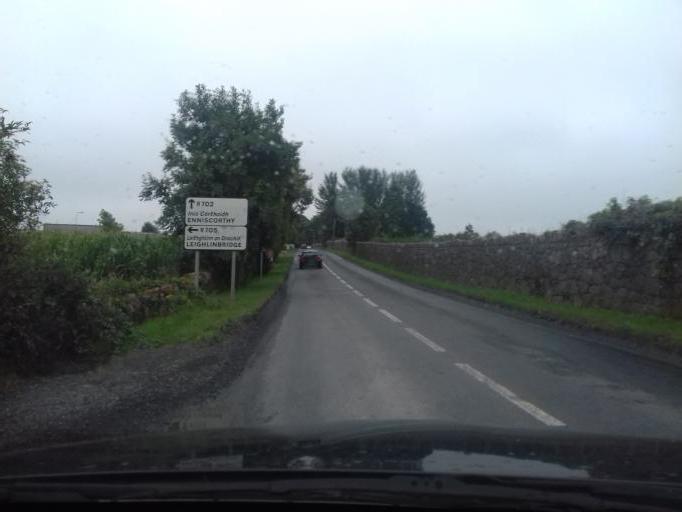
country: IE
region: Leinster
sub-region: Kilkenny
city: Graiguenamanagh
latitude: 52.6049
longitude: -6.9394
